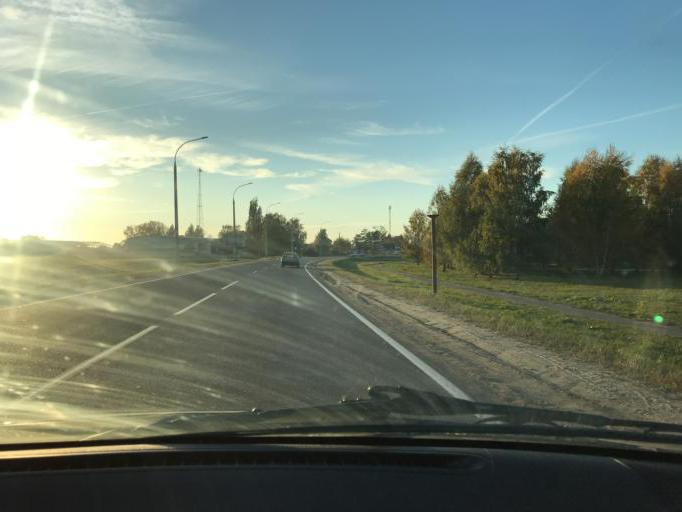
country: BY
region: Brest
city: Horad Kobryn
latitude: 52.2105
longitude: 24.3936
